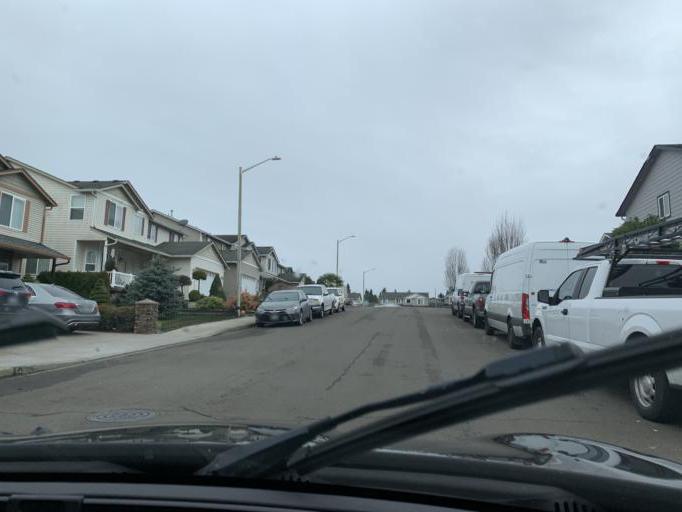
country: US
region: Washington
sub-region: Clark County
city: Five Corners
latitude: 45.6856
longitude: -122.5823
